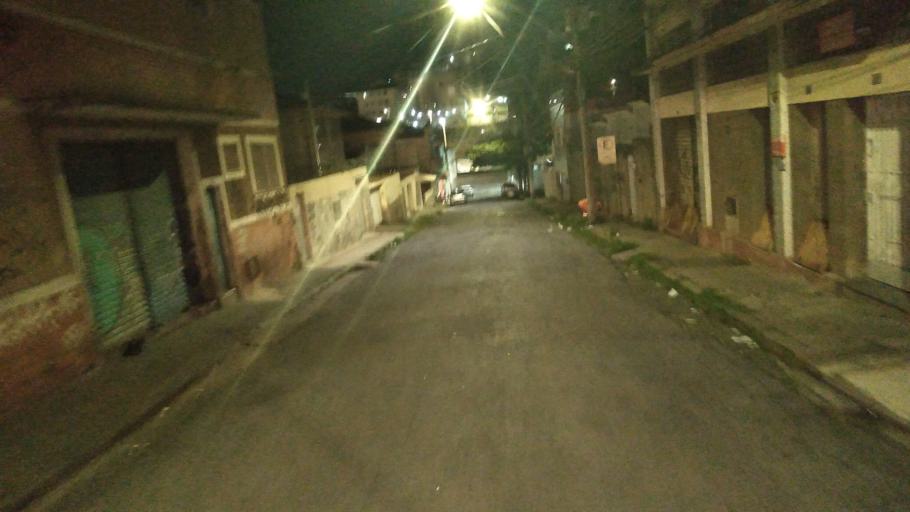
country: BR
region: Minas Gerais
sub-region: Belo Horizonte
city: Belo Horizonte
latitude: -19.9063
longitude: -43.9450
